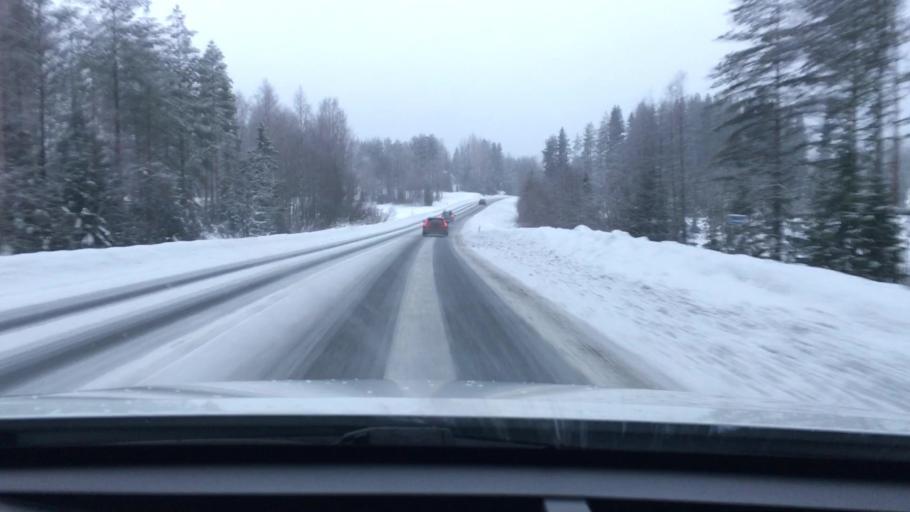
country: FI
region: Northern Savo
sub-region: Ylae-Savo
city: Sonkajaervi
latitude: 63.7642
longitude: 27.4096
